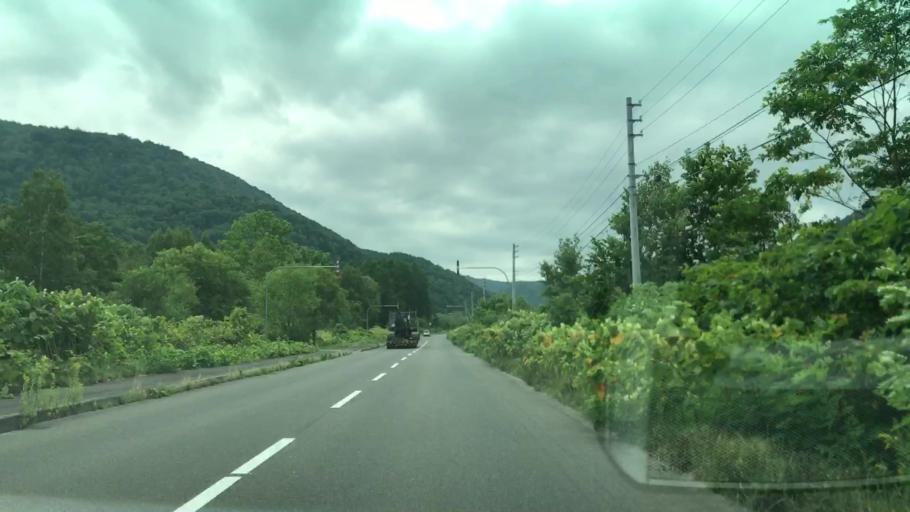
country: JP
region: Hokkaido
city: Yoichi
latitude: 43.0323
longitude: 140.8648
